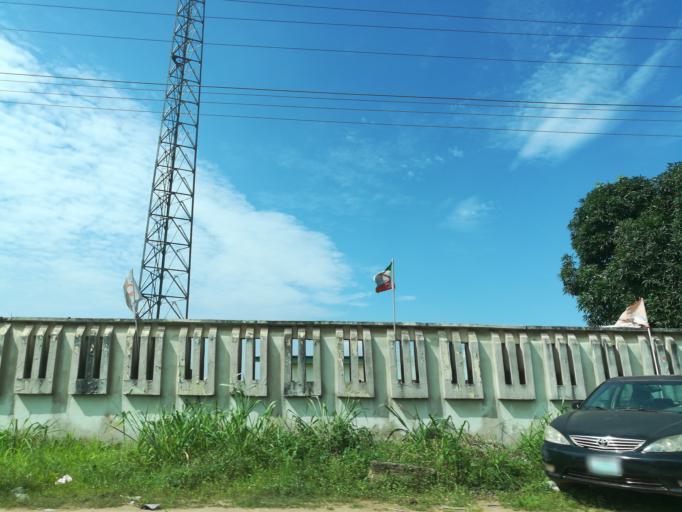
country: NG
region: Lagos
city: Ebute Ikorodu
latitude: 6.5970
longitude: 3.5012
